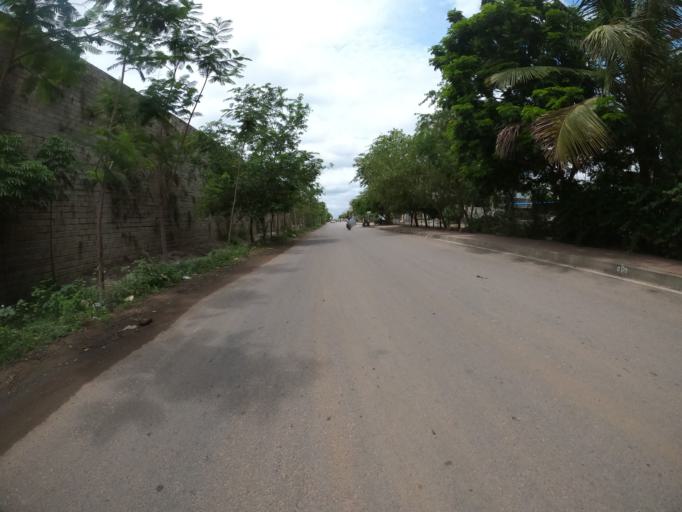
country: IN
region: Telangana
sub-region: Rangareddi
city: Sriramnagar
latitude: 17.2657
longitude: 78.3775
